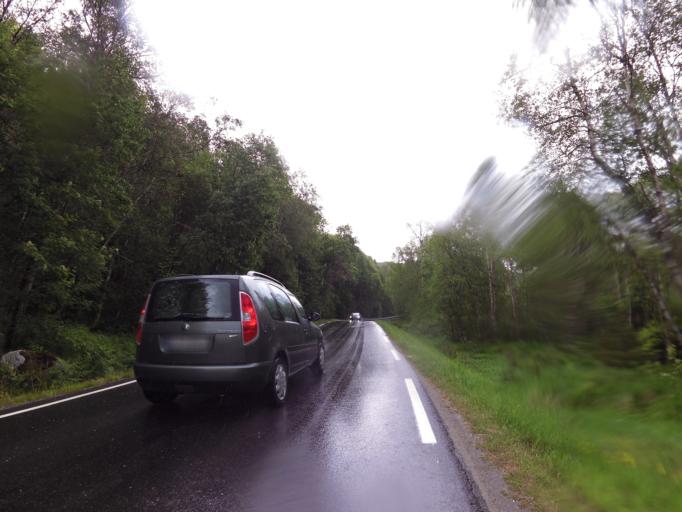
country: NO
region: Vest-Agder
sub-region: Lyngdal
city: Lyngdal
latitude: 58.1113
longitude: 7.0849
